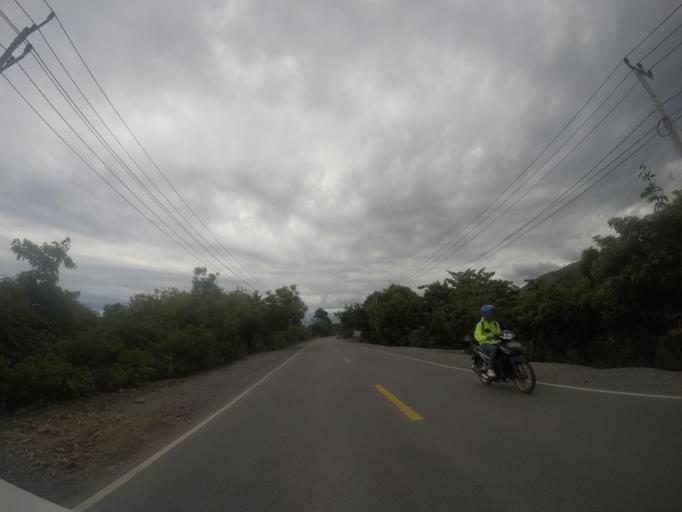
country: TL
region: Liquica
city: Liquica
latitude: -8.5643
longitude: 125.4139
